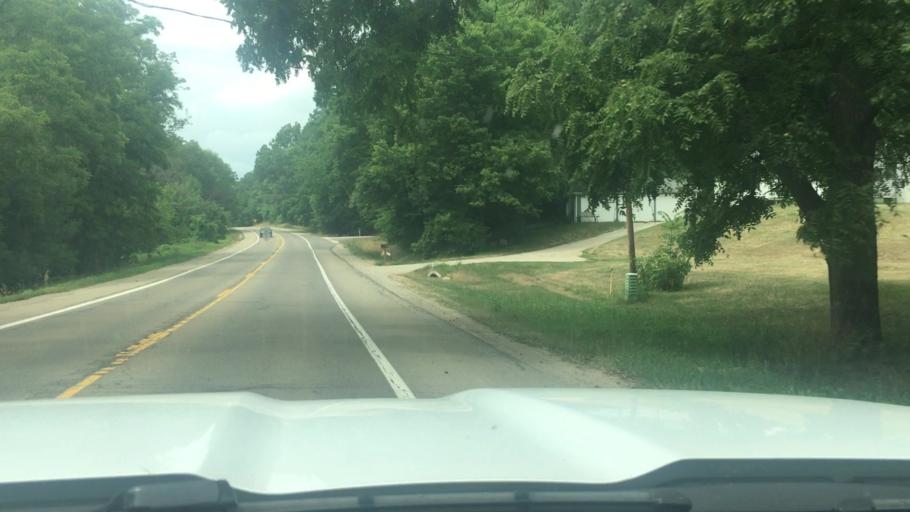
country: US
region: Michigan
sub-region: Kent County
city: Forest Hills
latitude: 42.9368
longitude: -85.4437
